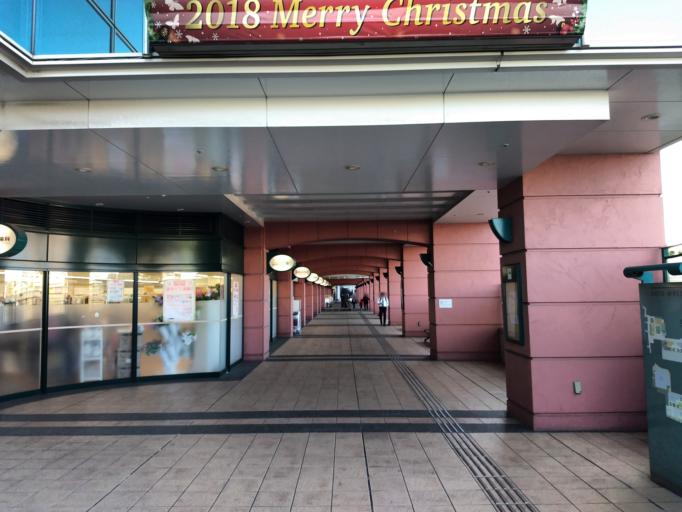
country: JP
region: Kanagawa
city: Yokohama
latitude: 35.4876
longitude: 139.6540
